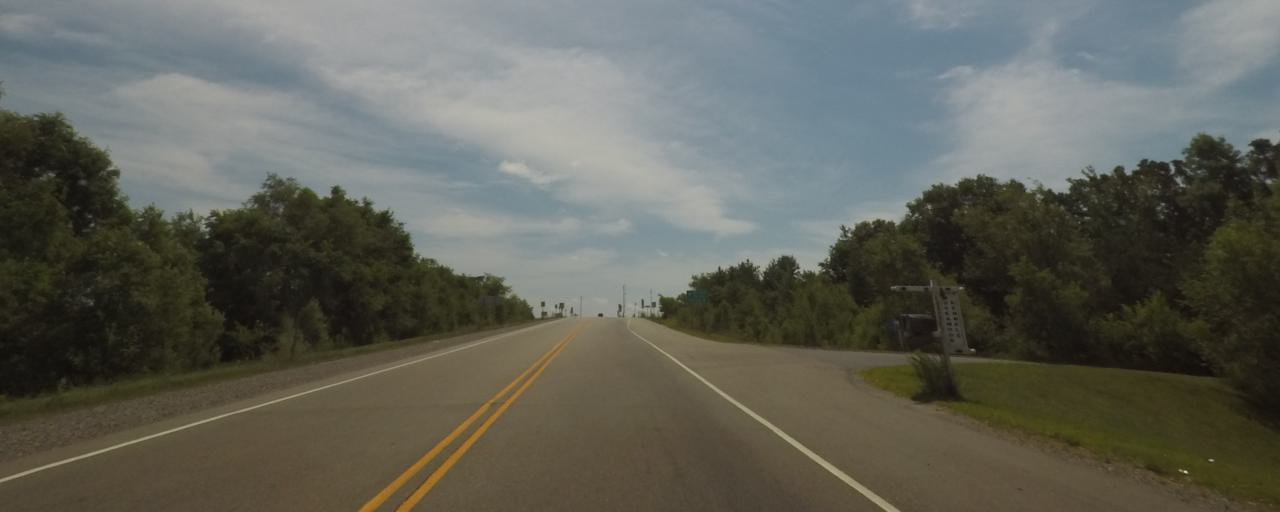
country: US
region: Wisconsin
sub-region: Portage County
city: Plover
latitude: 44.4328
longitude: -89.5218
